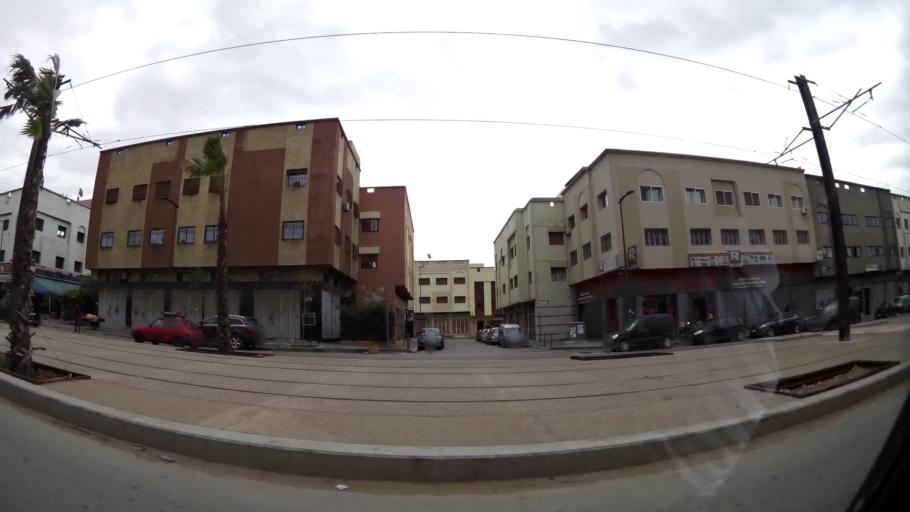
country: MA
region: Grand Casablanca
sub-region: Casablanca
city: Casablanca
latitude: 33.5729
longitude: -7.5788
